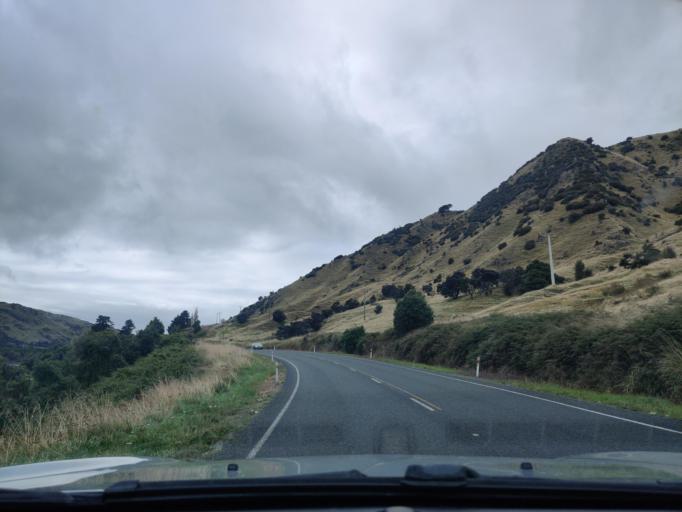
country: NZ
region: Canterbury
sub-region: Hurunui District
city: Amberley
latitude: -42.6697
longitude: 172.7667
